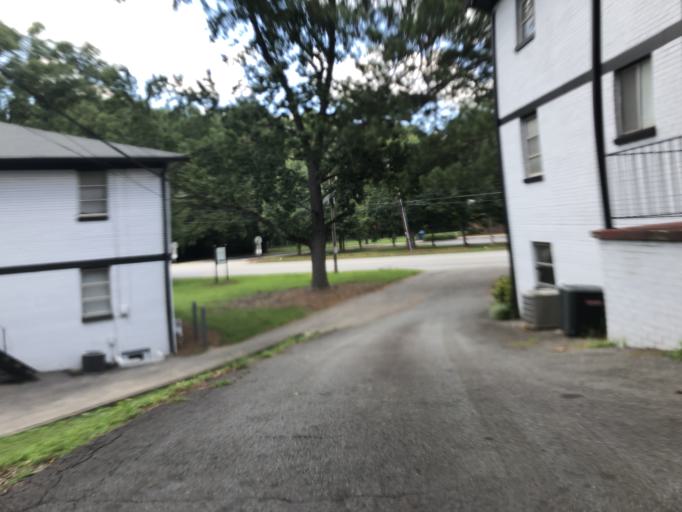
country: US
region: Georgia
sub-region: DeKalb County
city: North Decatur
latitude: 33.7825
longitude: -84.3055
